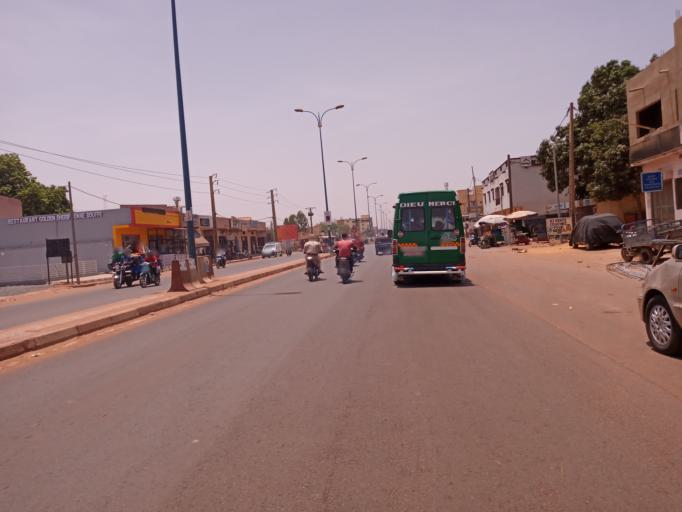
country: ML
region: Bamako
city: Bamako
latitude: 12.6055
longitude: -8.0482
